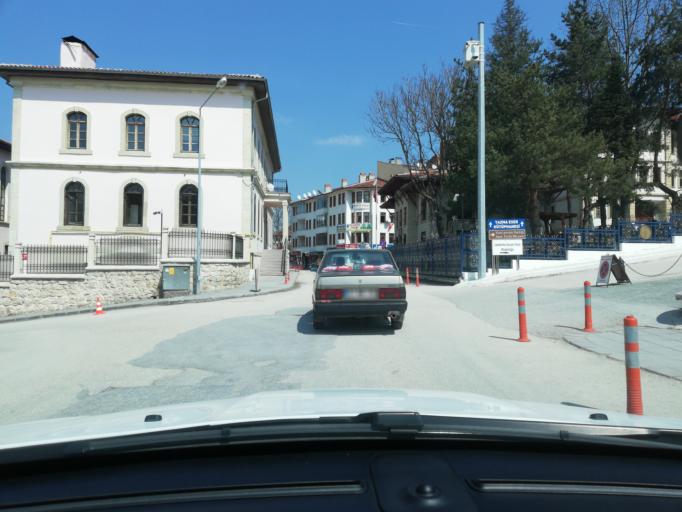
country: TR
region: Kastamonu
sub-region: Cide
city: Kastamonu
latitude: 41.3762
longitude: 33.7783
